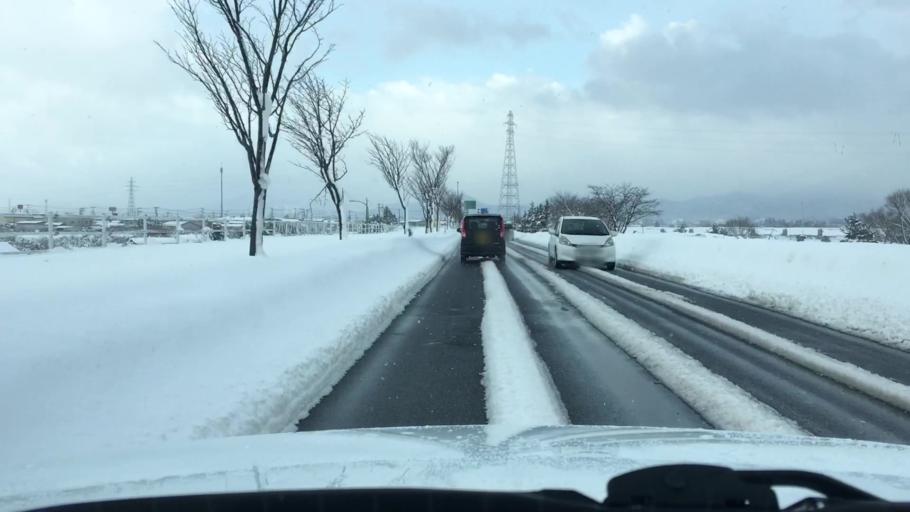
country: JP
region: Aomori
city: Hirosaki
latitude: 40.6312
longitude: 140.4733
